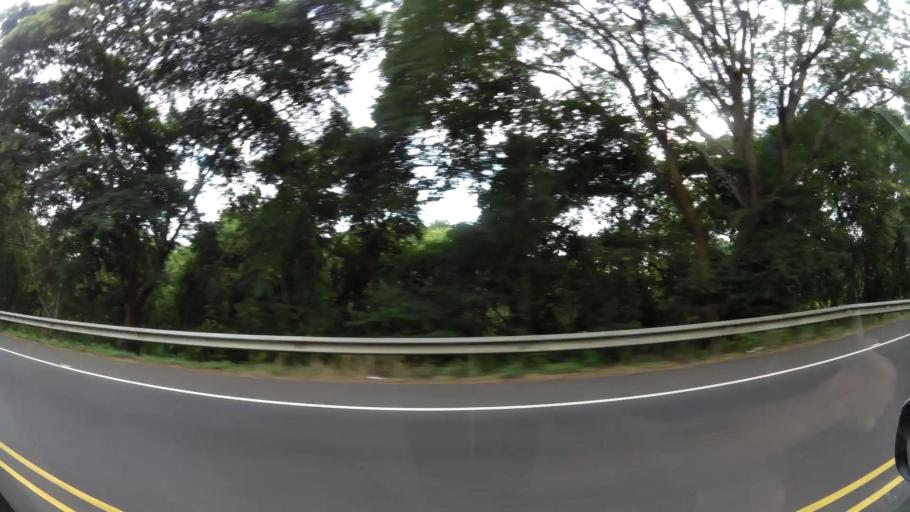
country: CR
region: Alajuela
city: Orotina
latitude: 9.8864
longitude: -84.5893
